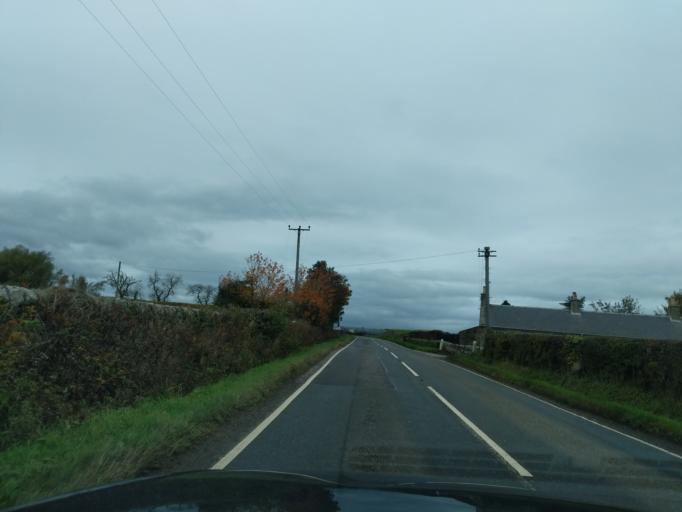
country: GB
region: Scotland
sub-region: Fife
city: Saint Andrews
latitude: 56.2989
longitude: -2.7524
